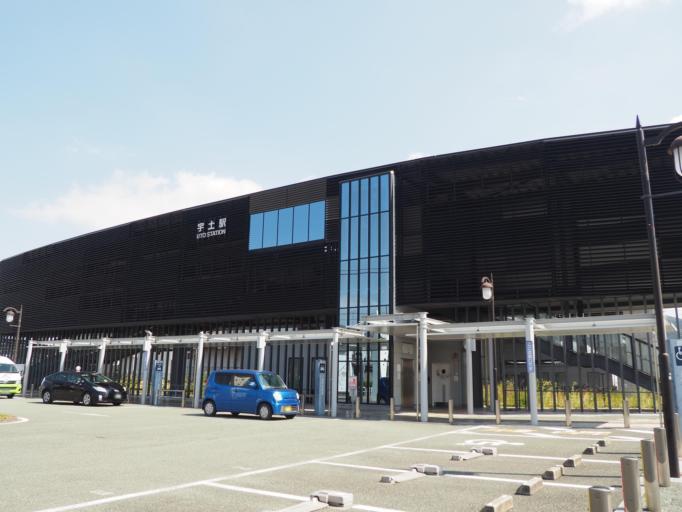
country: JP
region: Kumamoto
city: Uto
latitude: 32.6938
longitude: 130.6685
